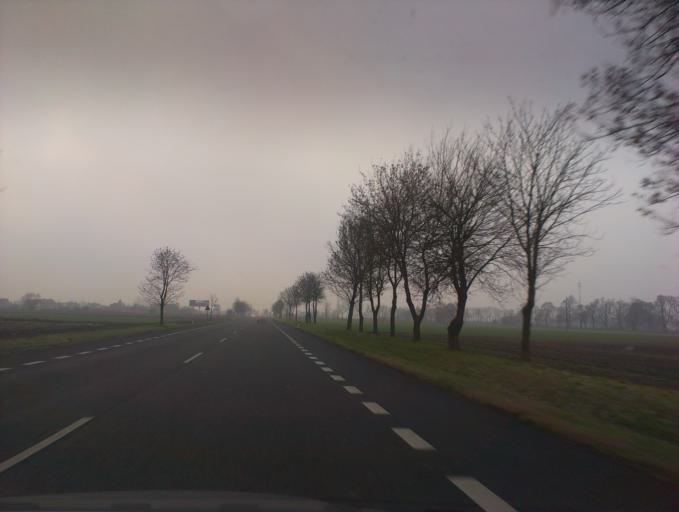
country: PL
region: Greater Poland Voivodeship
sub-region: Powiat chodzieski
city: Budzyn
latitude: 52.8960
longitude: 16.9698
